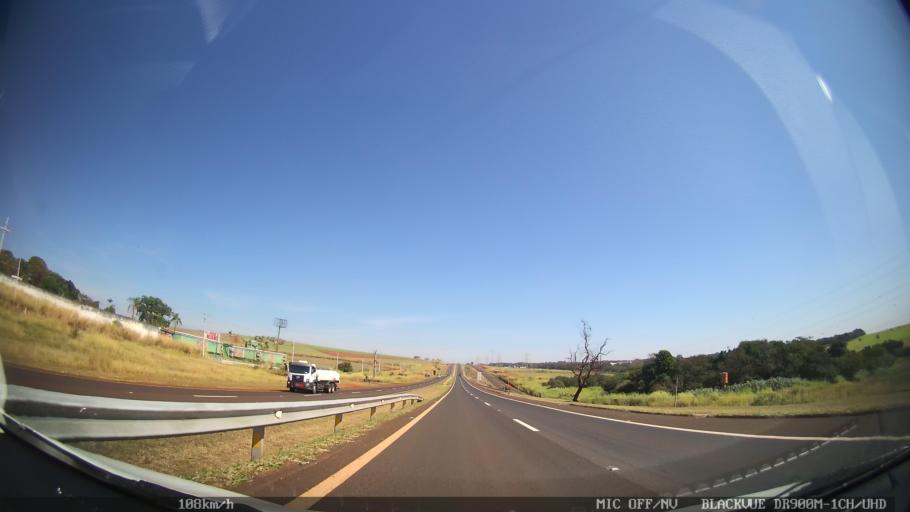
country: BR
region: Sao Paulo
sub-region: Ribeirao Preto
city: Ribeirao Preto
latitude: -21.1393
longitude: -47.8657
